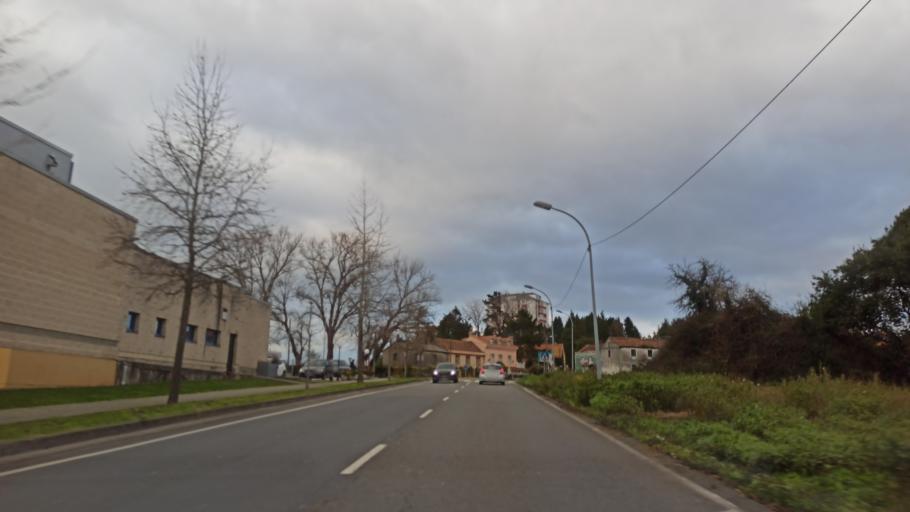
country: ES
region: Galicia
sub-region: Provincia da Coruna
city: Oleiros
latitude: 43.3411
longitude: -8.3457
